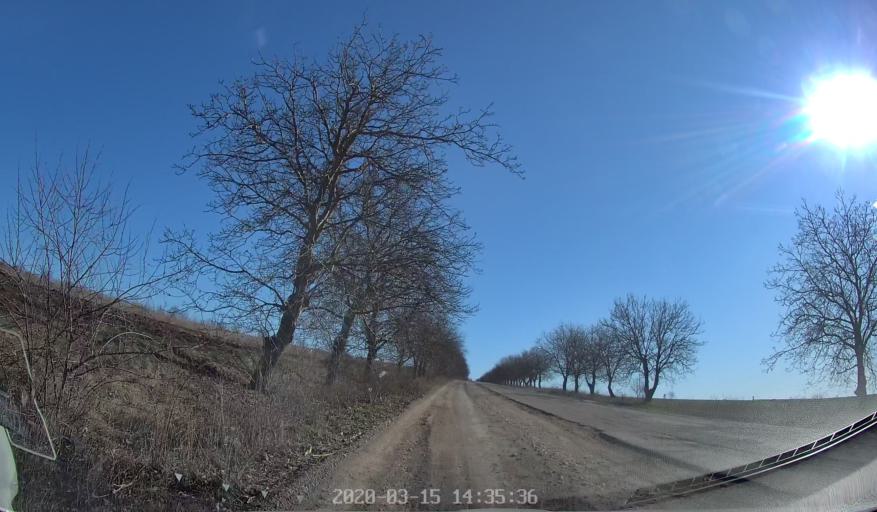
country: MD
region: Orhei
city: Orhei
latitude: 47.3287
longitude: 28.9248
